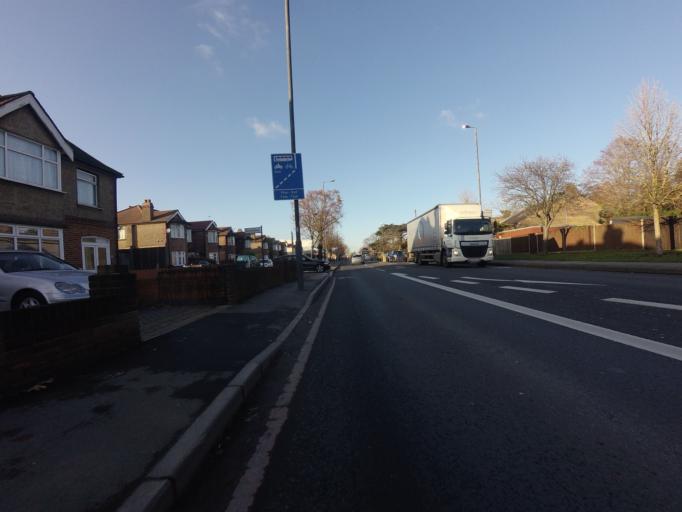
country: GB
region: England
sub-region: Greater London
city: Feltham
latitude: 51.4542
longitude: -0.4076
